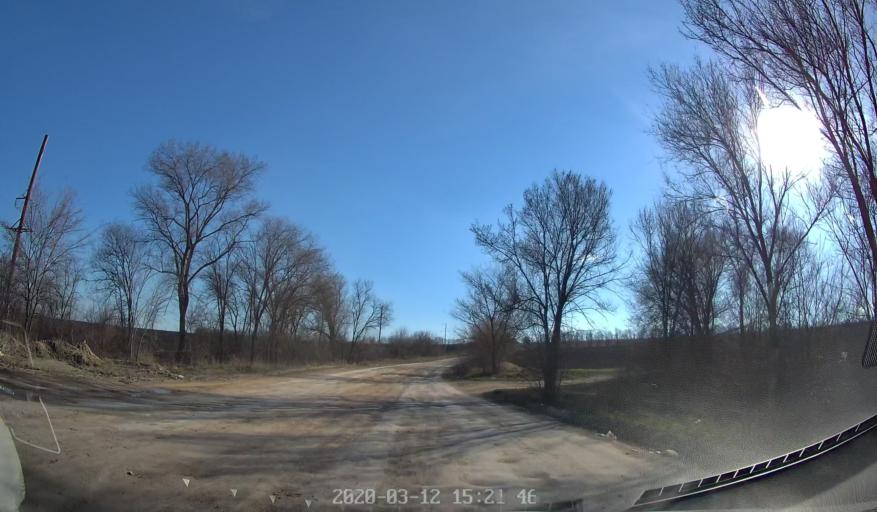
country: MD
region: Chisinau
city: Ciorescu
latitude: 47.2007
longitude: 28.9213
